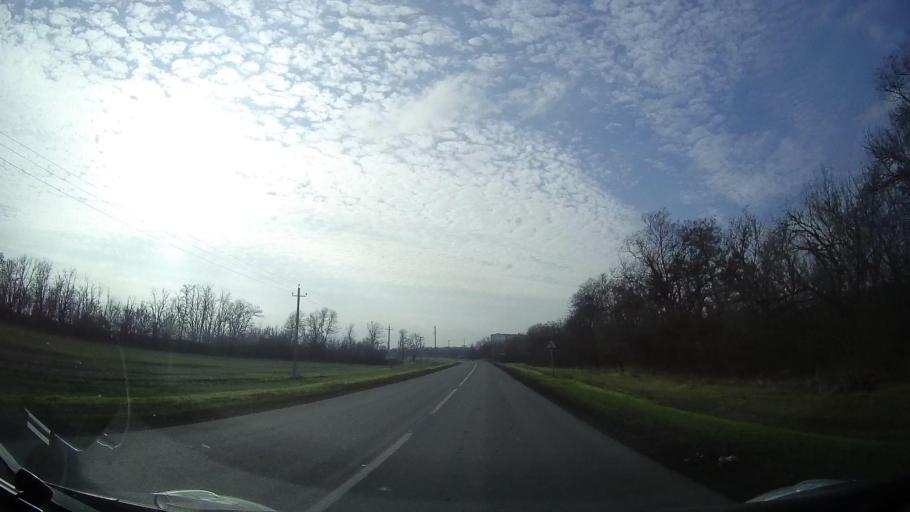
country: RU
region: Rostov
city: Mechetinskaya
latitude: 46.7930
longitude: 40.4974
